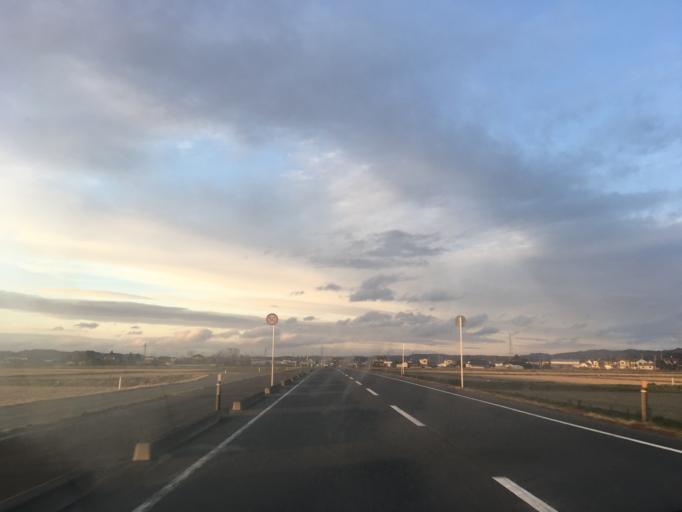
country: JP
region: Miyagi
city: Wakuya
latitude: 38.7027
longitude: 141.2602
